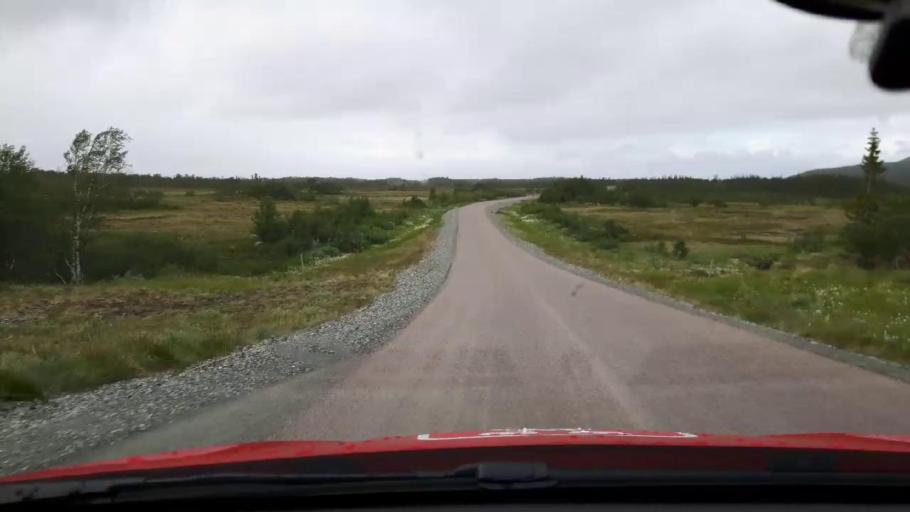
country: SE
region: Jaemtland
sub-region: Are Kommun
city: Are
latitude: 63.2214
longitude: 12.4142
